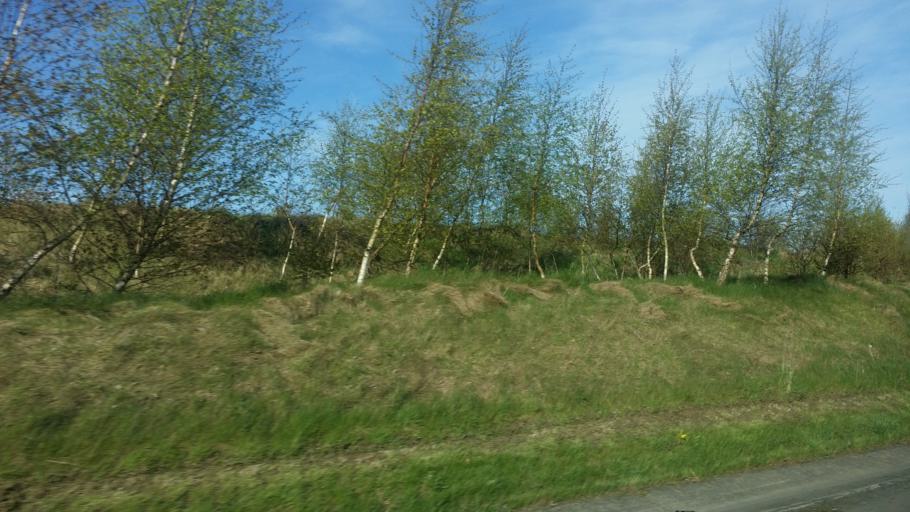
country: IE
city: Kentstown
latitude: 53.5952
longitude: -6.5878
